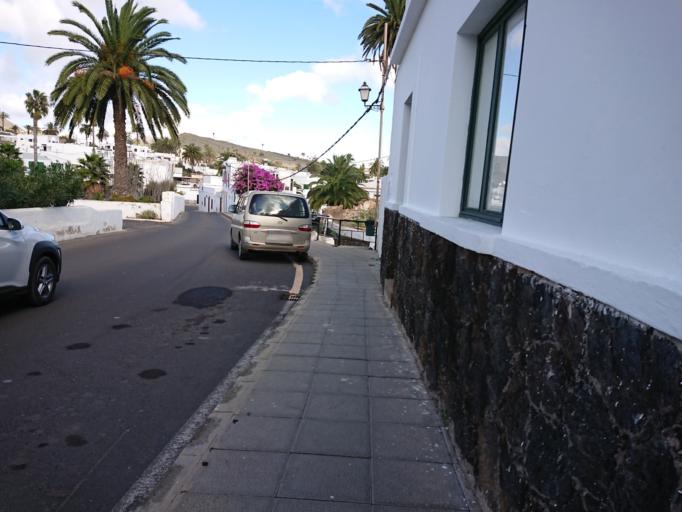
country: ES
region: Canary Islands
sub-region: Provincia de Las Palmas
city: Haria
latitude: 29.1449
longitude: -13.5018
